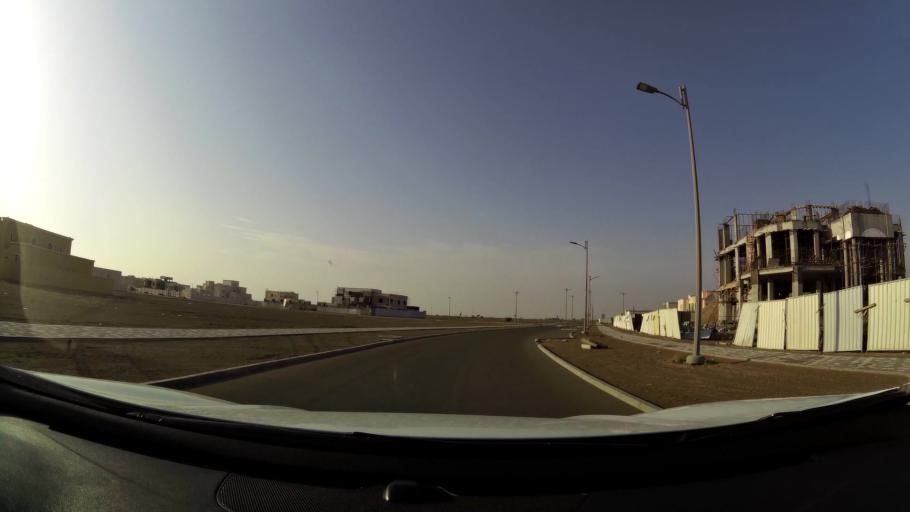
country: AE
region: Abu Dhabi
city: Al Ain
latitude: 24.1108
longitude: 55.8550
